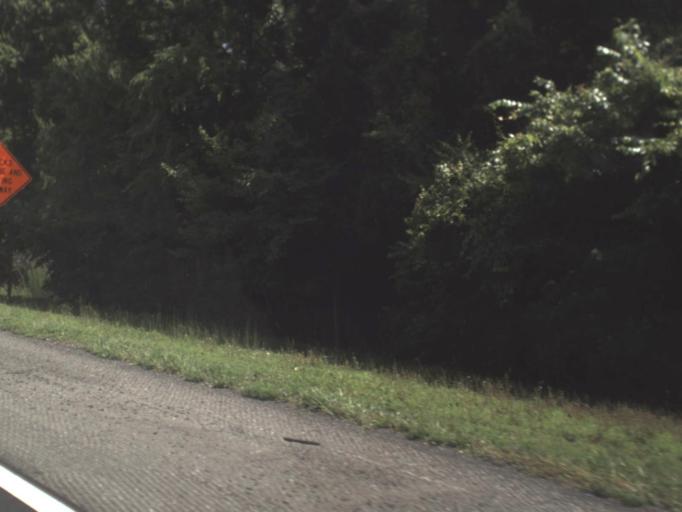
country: US
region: Florida
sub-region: Nassau County
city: Yulee
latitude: 30.5551
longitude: -81.6406
